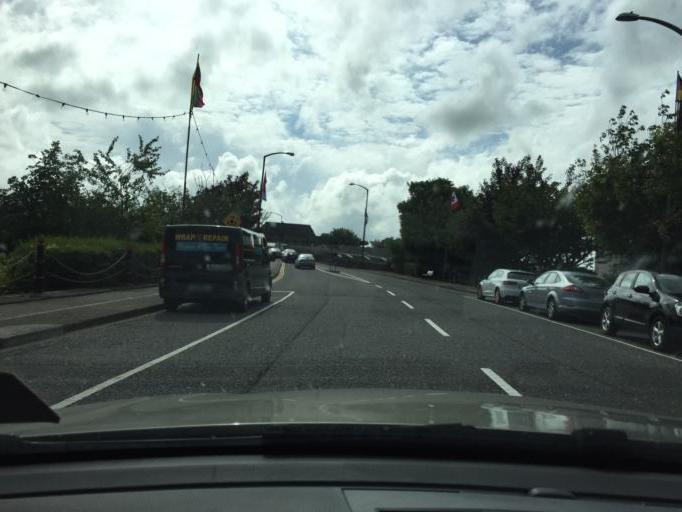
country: IE
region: Munster
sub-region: Waterford
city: Dungarvan
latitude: 52.0917
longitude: -7.6187
